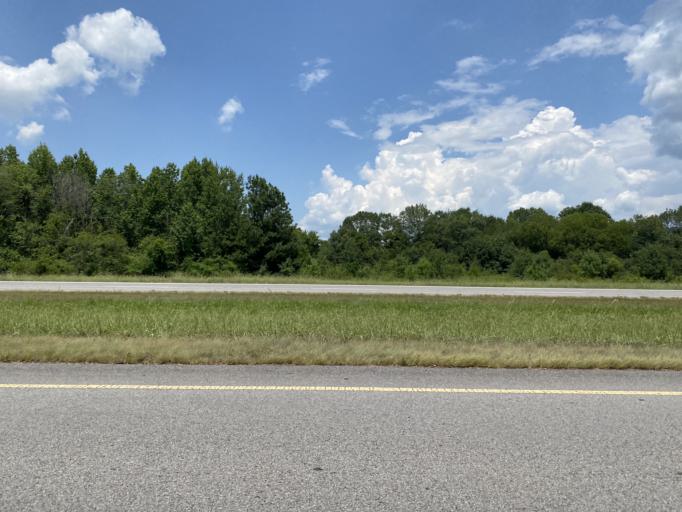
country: US
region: Alabama
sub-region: Jackson County
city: Scottsboro
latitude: 34.6202
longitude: -86.1027
